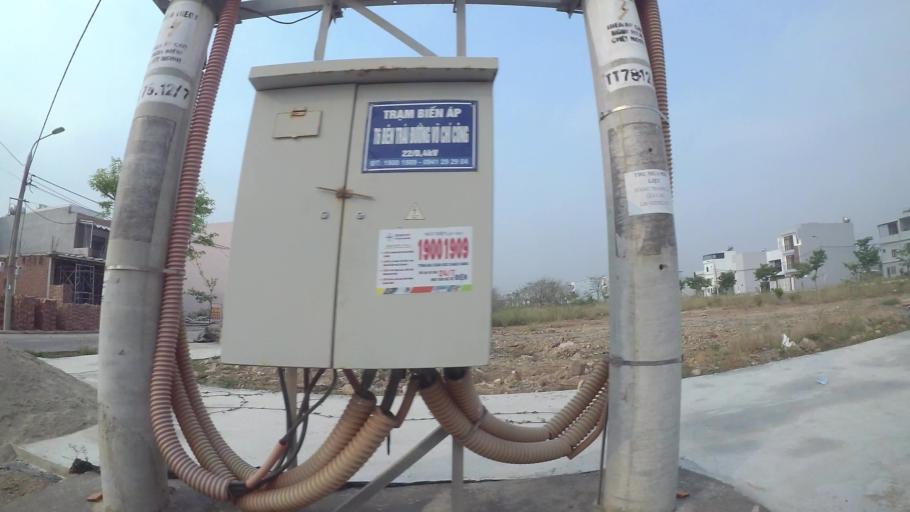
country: VN
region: Da Nang
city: Cam Le
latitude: 16.0157
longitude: 108.2206
